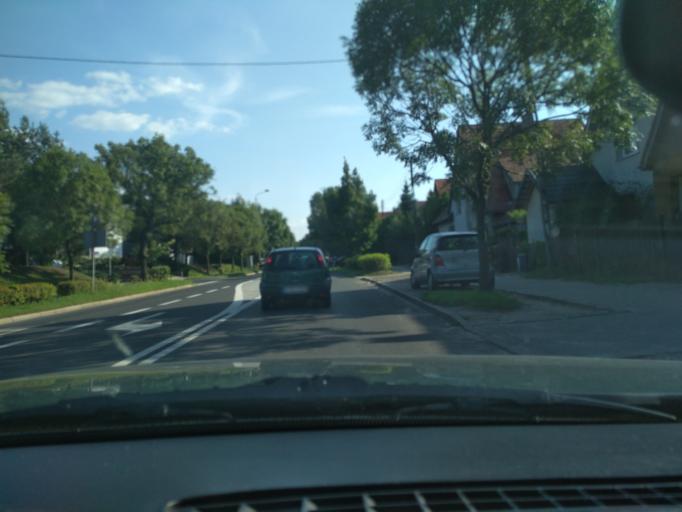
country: PL
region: Silesian Voivodeship
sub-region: Gliwice
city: Gliwice
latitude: 50.2826
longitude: 18.6626
